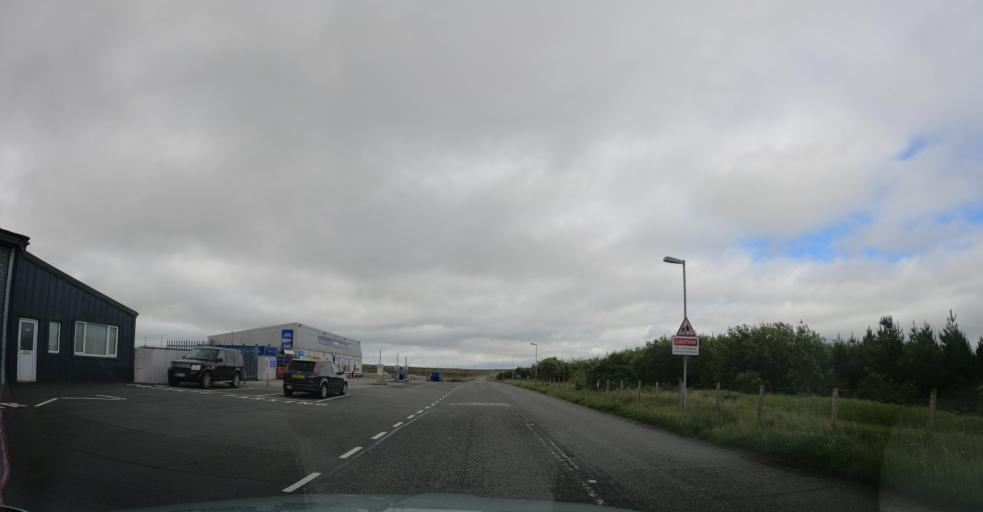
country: GB
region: Scotland
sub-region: Eilean Siar
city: Stornoway
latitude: 58.1575
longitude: -6.4962
